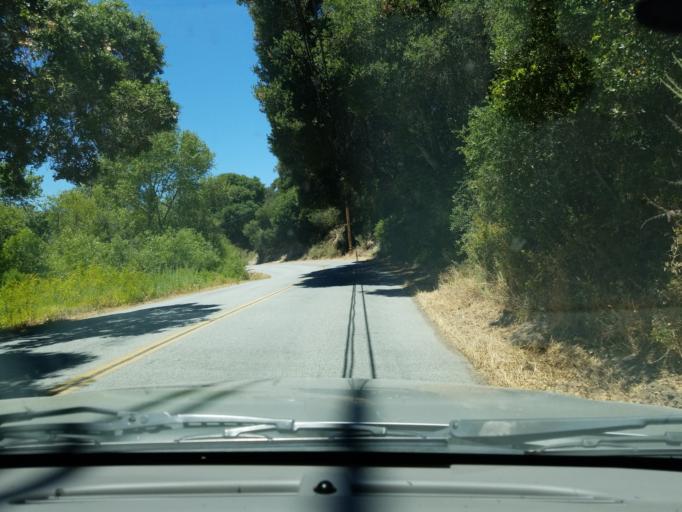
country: US
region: California
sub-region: Monterey County
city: Carmel Valley Village
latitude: 36.4548
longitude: -121.7038
